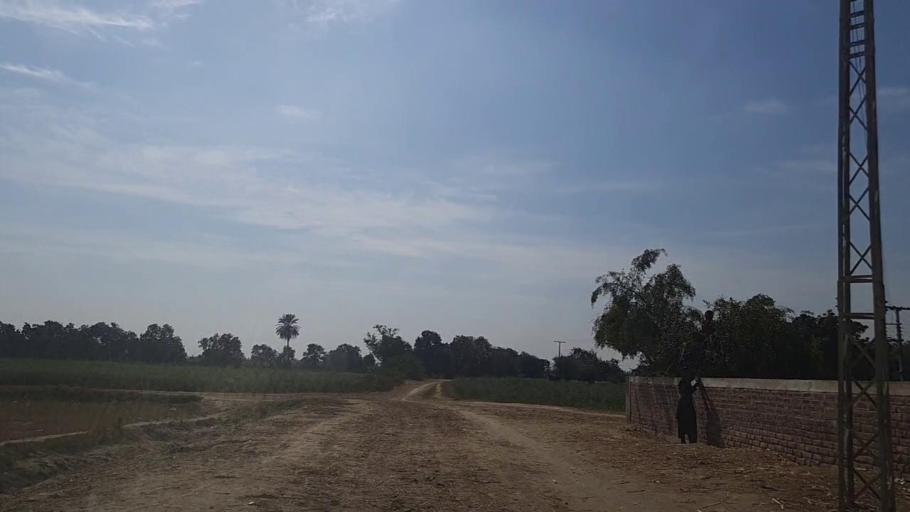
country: PK
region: Sindh
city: Mirpur Khas
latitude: 25.4665
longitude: 68.9625
